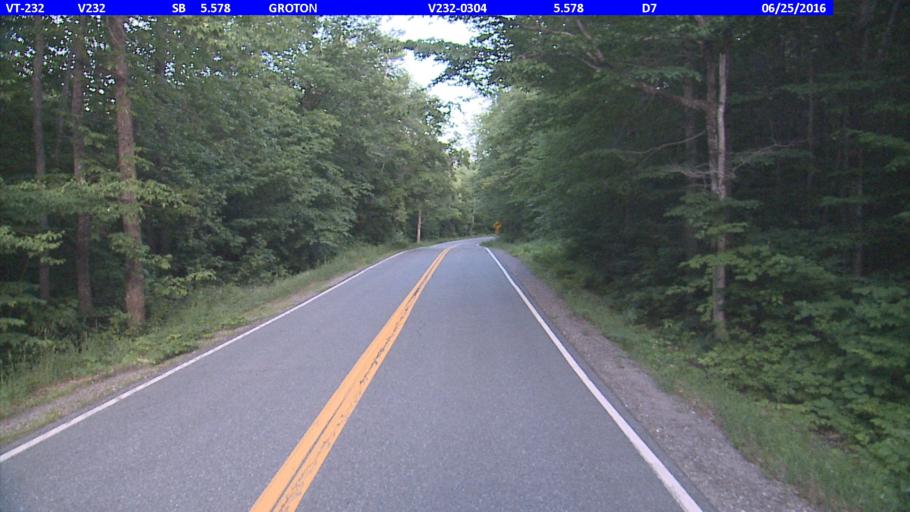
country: US
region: Vermont
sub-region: Washington County
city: Barre
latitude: 44.2791
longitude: -72.2872
